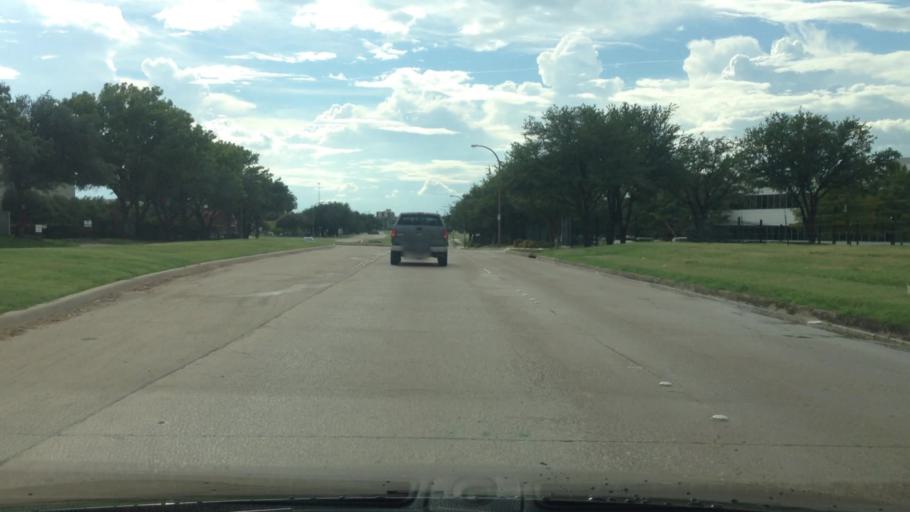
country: US
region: Texas
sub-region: Tarrant County
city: Haltom City
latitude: 32.8243
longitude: -97.3015
